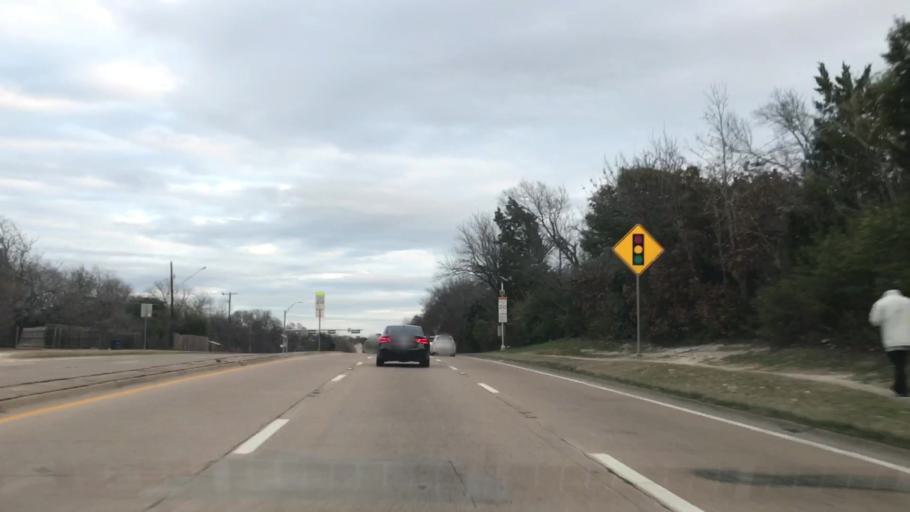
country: US
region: Texas
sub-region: Dallas County
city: Cockrell Hill
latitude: 32.6912
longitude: -96.8540
